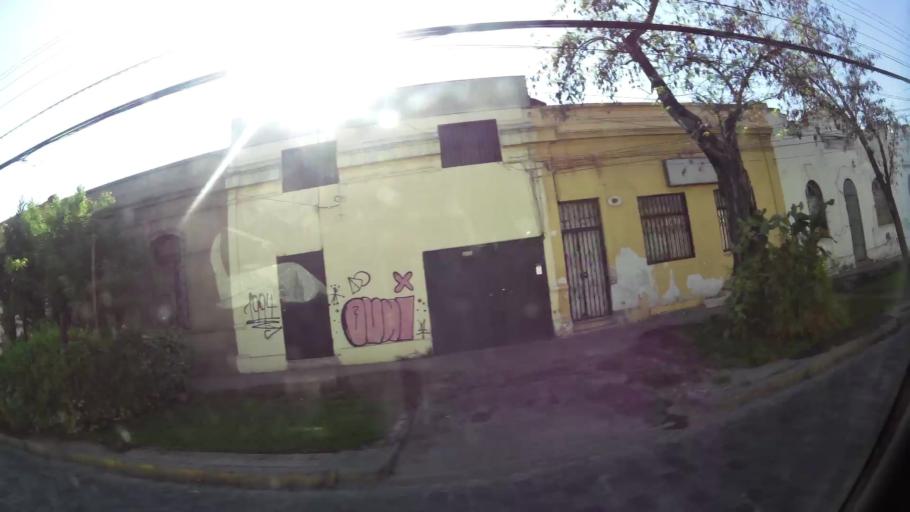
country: CL
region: Santiago Metropolitan
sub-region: Provincia de Santiago
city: Santiago
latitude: -33.4617
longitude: -70.6318
